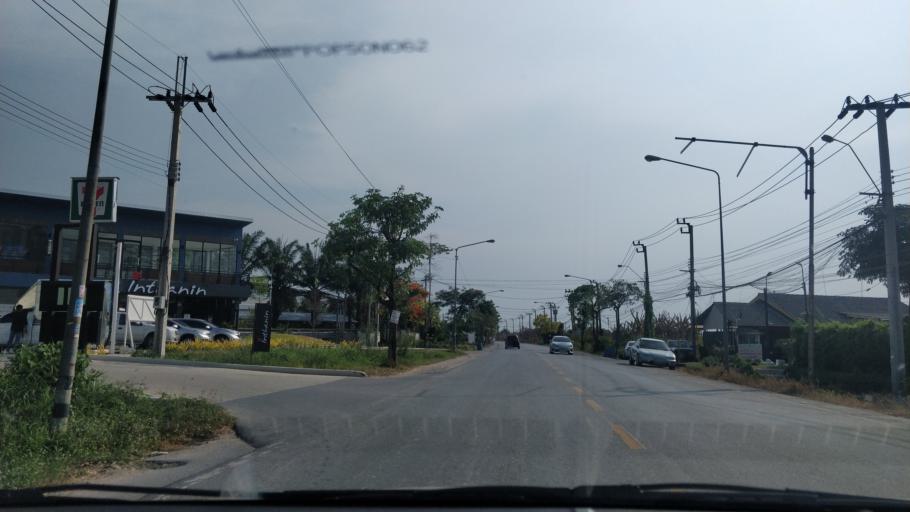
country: TH
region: Bangkok
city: Saphan Sung
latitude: 13.7535
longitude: 100.7200
